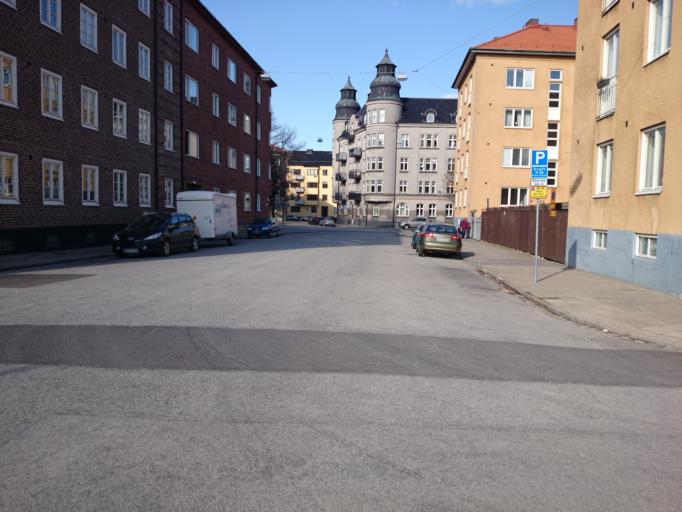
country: SE
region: Skane
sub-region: Malmo
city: Malmoe
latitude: 55.5886
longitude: 13.0180
